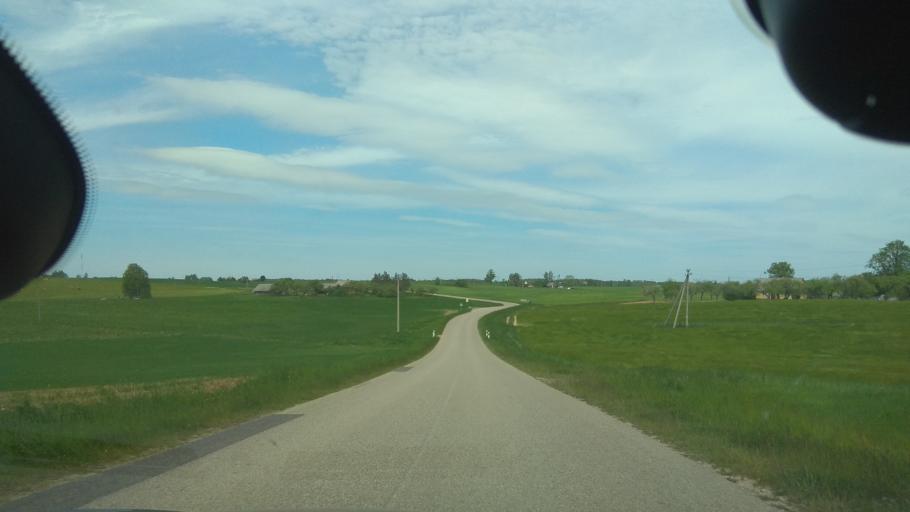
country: LT
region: Vilnius County
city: Ukmerge
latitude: 55.1579
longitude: 24.5436
